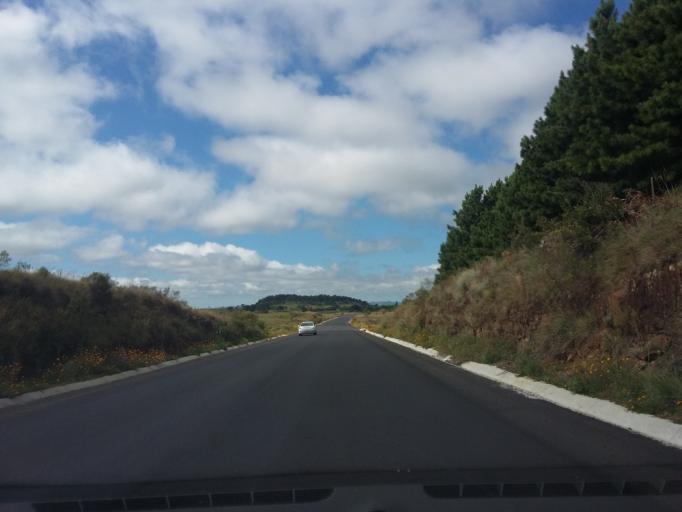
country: BR
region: Santa Catarina
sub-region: Sao Joaquim
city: Sao Joaquim
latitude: -28.0303
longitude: -50.0773
